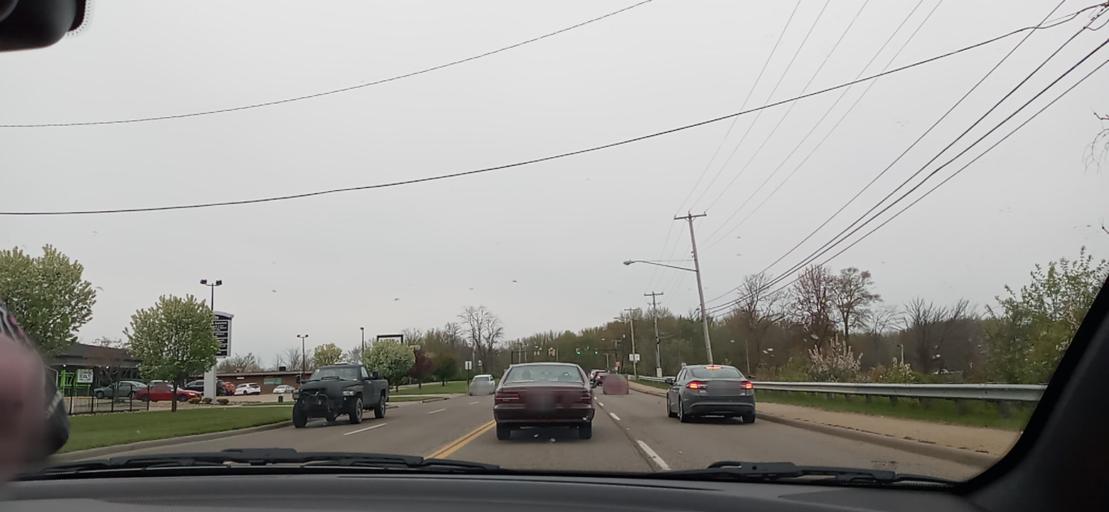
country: US
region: Ohio
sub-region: Summit County
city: Portage Lakes
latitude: 41.0256
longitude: -81.5485
